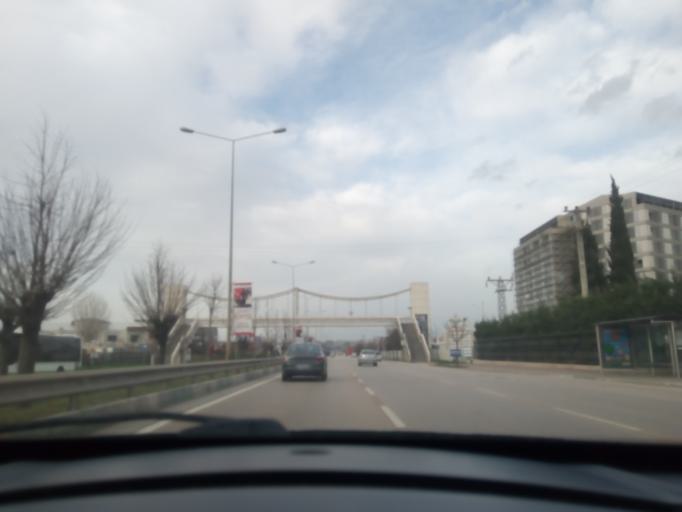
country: TR
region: Bursa
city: Cali
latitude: 40.2146
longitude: 28.9041
